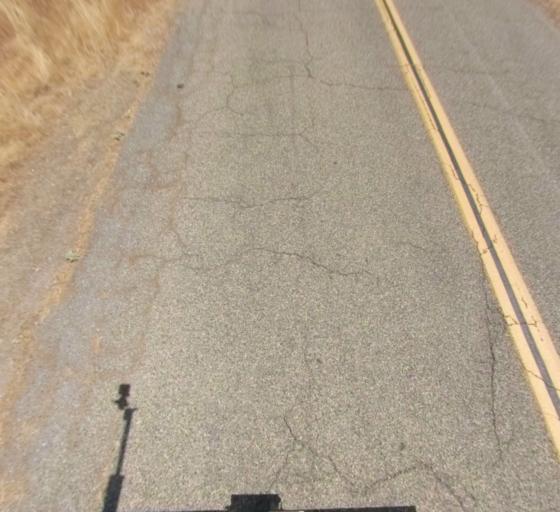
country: US
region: California
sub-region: Fresno County
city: Auberry
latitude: 37.1518
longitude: -119.5121
